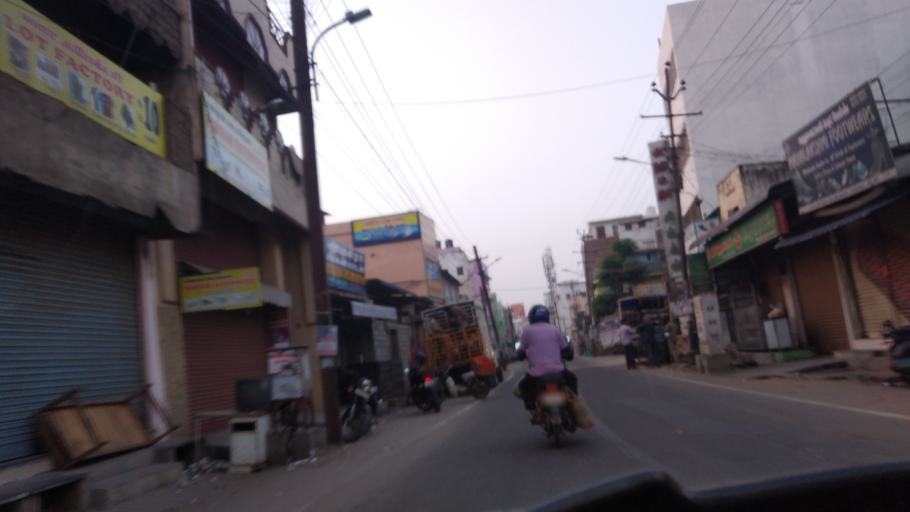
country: IN
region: Tamil Nadu
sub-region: Coimbatore
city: Coimbatore
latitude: 10.9996
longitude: 76.9599
